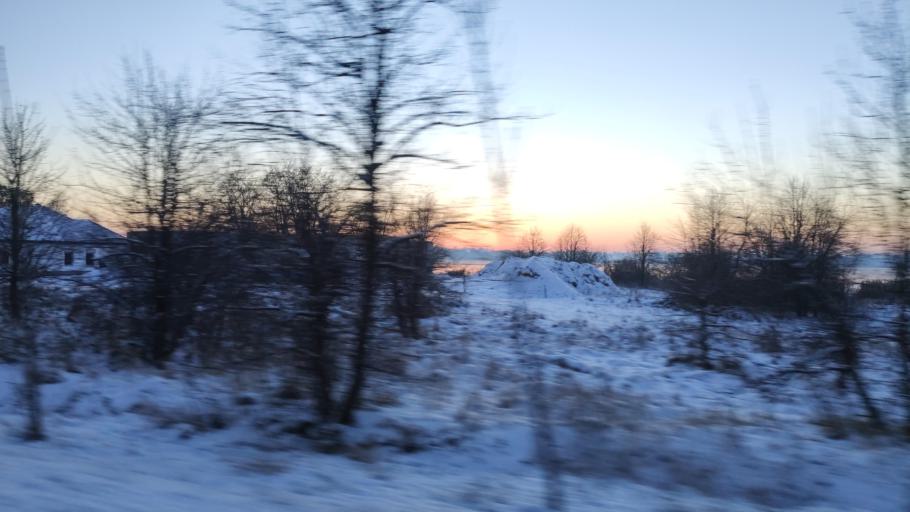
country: PL
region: Kujawsko-Pomorskie
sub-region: Powiat zninski
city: Barcin
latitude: 52.8716
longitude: 17.9007
